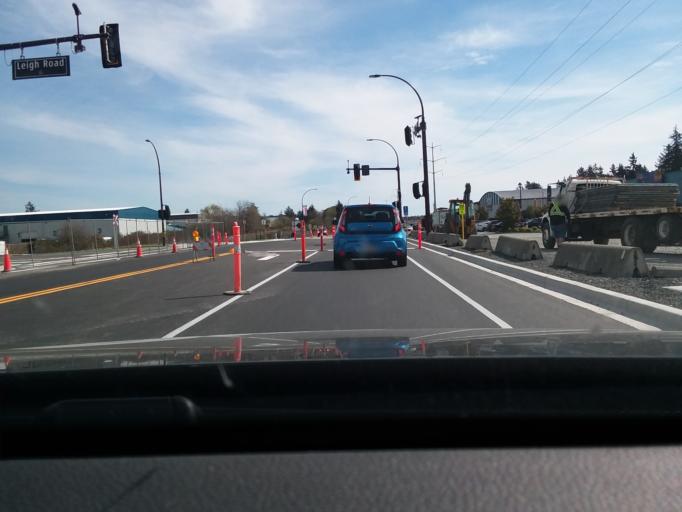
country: CA
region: British Columbia
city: Langford
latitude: 48.4437
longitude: -123.5234
